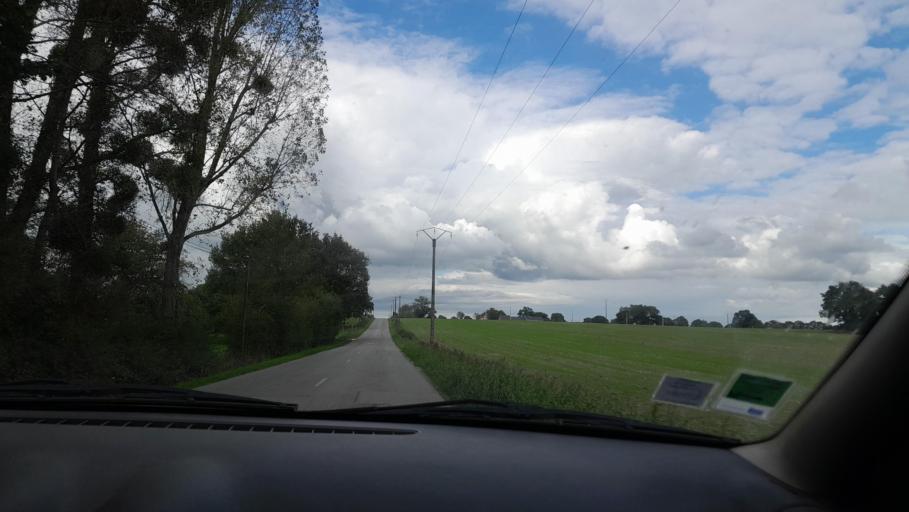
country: FR
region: Brittany
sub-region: Departement d'Ille-et-Vilaine
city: Le Pertre
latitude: 47.9964
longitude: -1.0399
